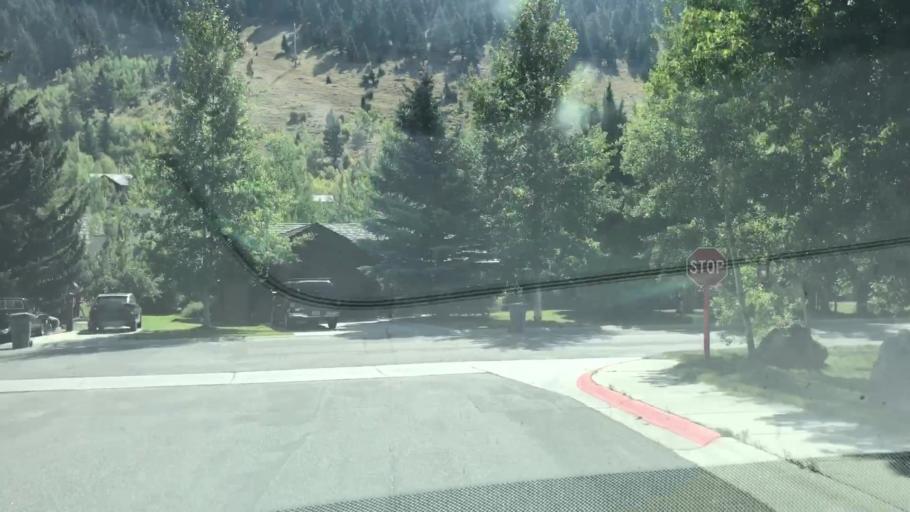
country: US
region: Wyoming
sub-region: Teton County
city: Jackson
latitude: 43.4636
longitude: -110.7916
